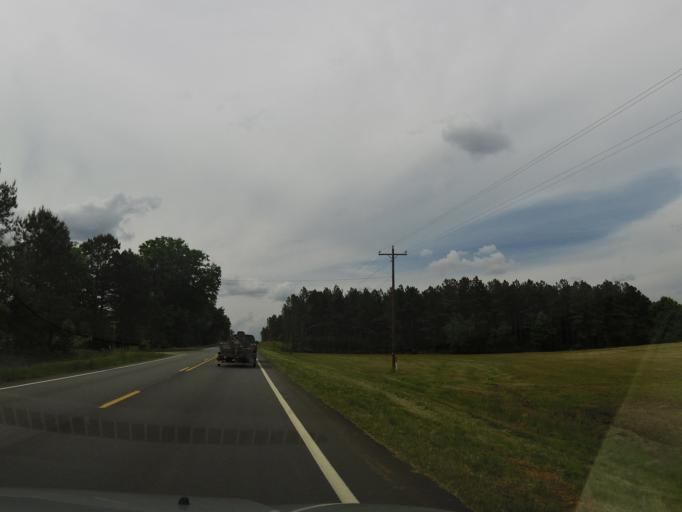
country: US
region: Georgia
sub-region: McDuffie County
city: Thomson
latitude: 33.3860
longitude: -82.4728
